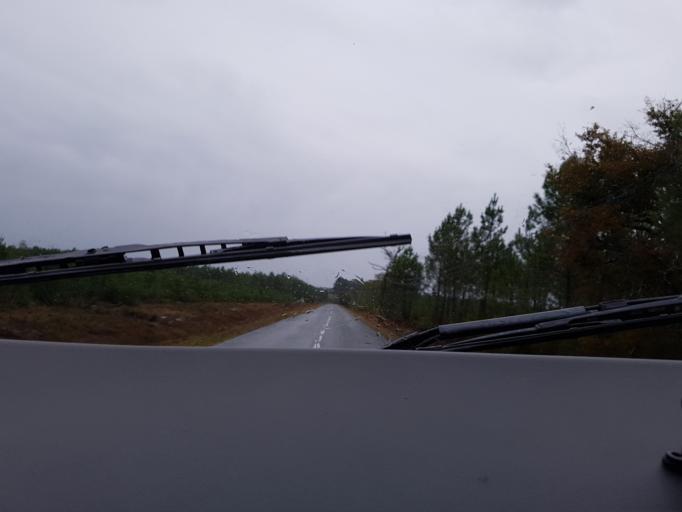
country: FR
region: Aquitaine
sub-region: Departement de la Gironde
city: Saint-Symphorien
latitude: 44.3561
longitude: -0.6275
